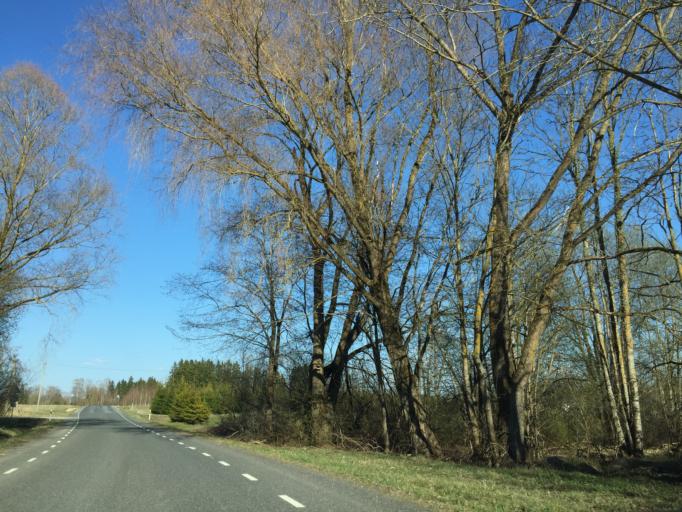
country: EE
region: Valgamaa
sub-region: Torva linn
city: Torva
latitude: 58.2372
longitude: 25.8839
